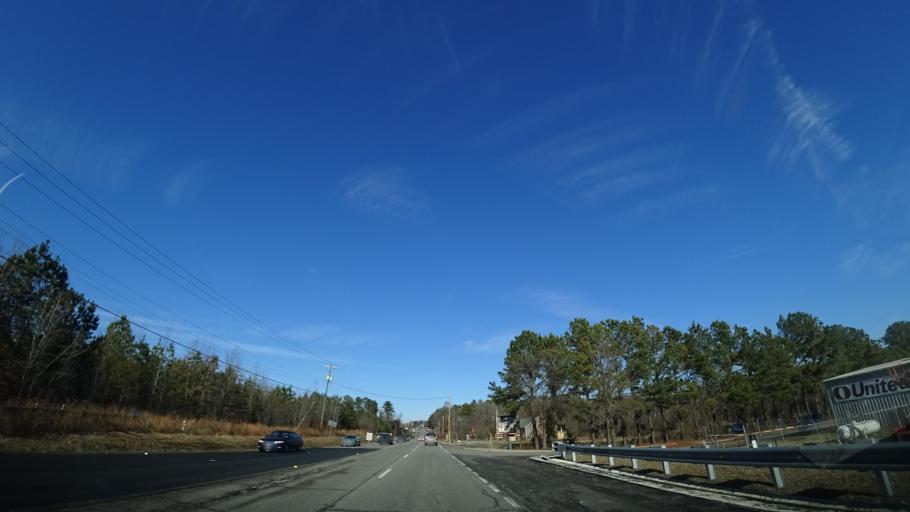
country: US
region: Virginia
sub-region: Henrico County
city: Glen Allen
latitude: 37.6927
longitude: -77.4630
